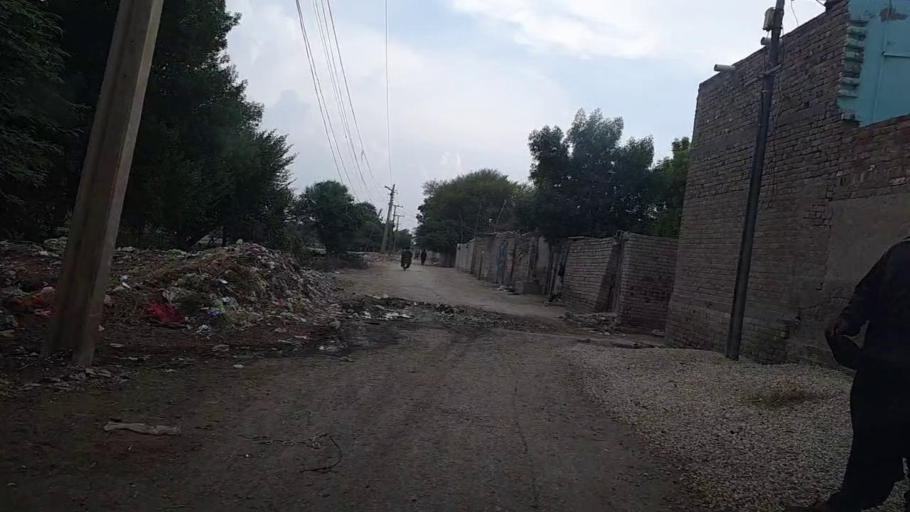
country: PK
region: Sindh
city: Khanpur
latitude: 27.8450
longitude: 69.4173
